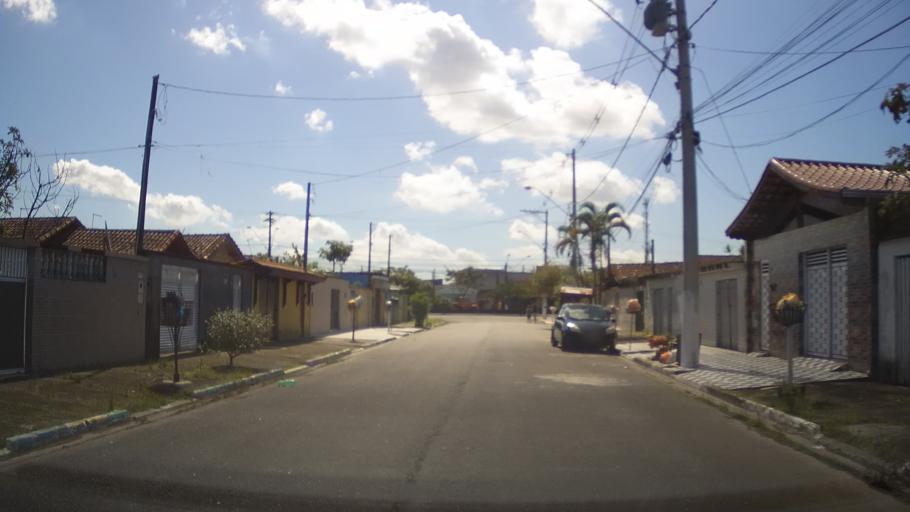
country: BR
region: Sao Paulo
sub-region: Mongagua
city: Mongagua
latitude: -24.0300
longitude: -46.5306
